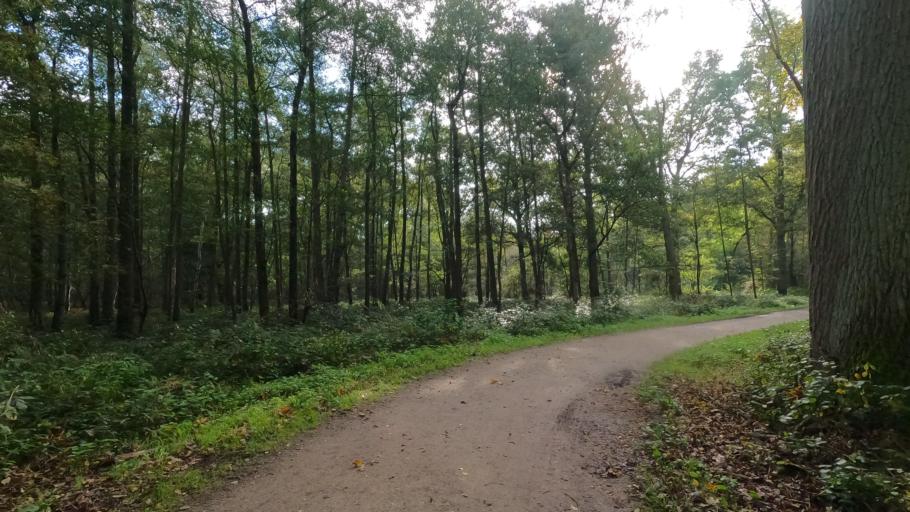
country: BE
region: Flanders
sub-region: Provincie Antwerpen
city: Heist-op-den-Berg
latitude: 51.0933
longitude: 4.7143
